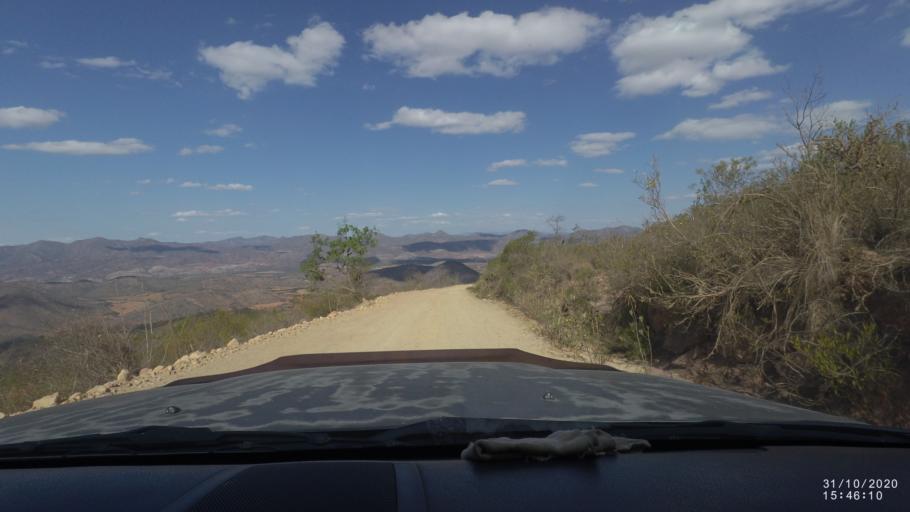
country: BO
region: Chuquisaca
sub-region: Provincia Zudanez
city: Mojocoya
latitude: -18.3158
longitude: -64.7176
